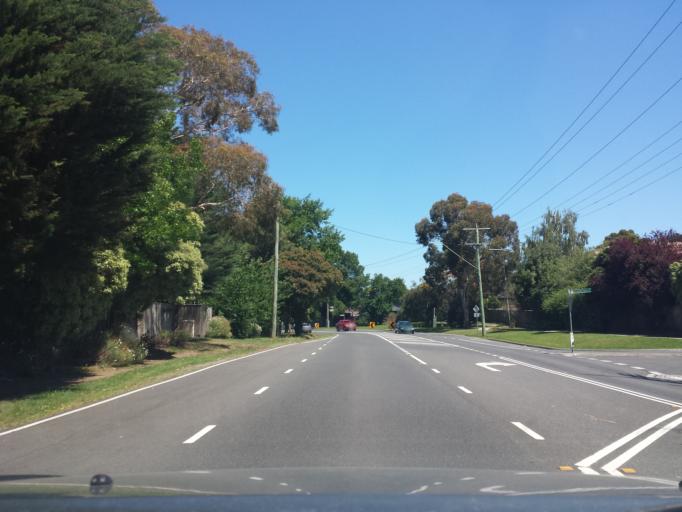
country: AU
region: Victoria
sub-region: Casey
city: Berwick
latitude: -38.0225
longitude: 145.3455
